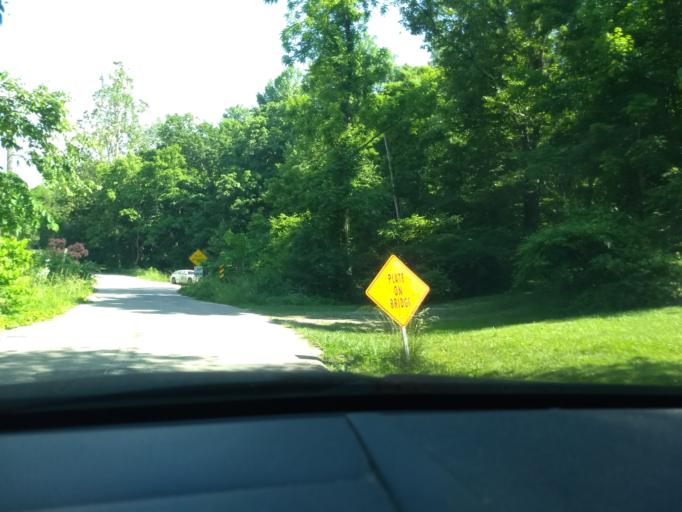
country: US
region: Indiana
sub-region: Floyd County
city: New Albany
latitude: 38.2673
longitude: -85.8660
